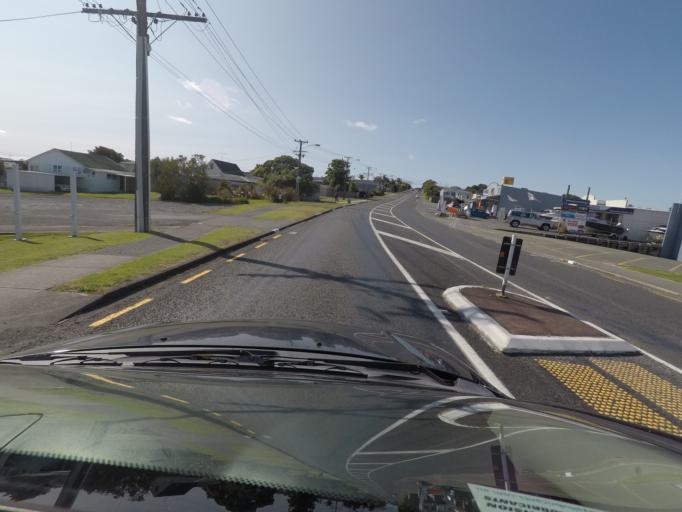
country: NZ
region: Auckland
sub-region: Auckland
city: Warkworth
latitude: -36.4230
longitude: 174.7265
